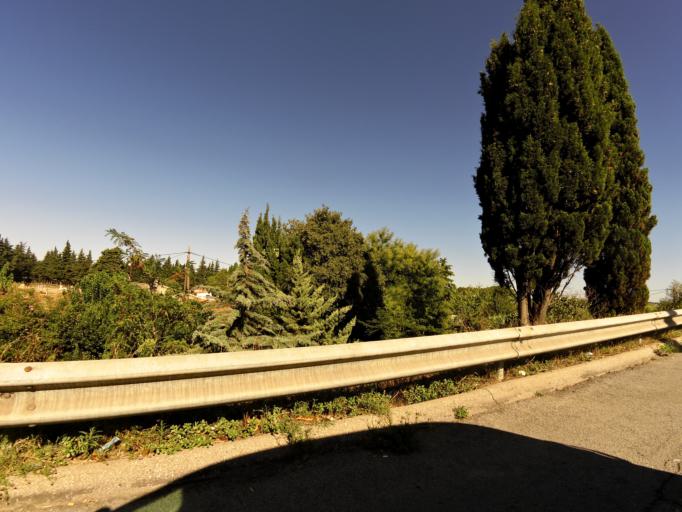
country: FR
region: Languedoc-Roussillon
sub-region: Departement du Gard
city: Nimes
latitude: 43.8172
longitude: 4.3669
